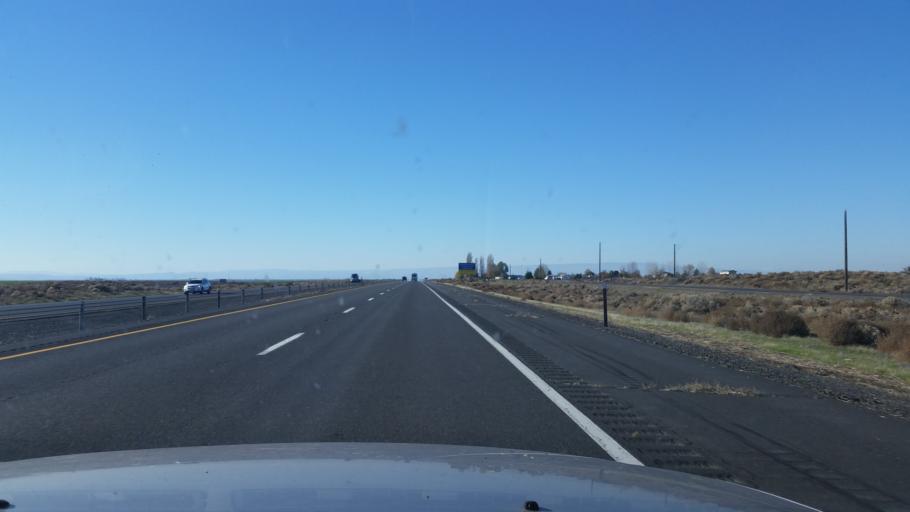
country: US
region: Washington
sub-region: Grant County
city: Royal City
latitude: 47.1040
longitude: -119.5958
